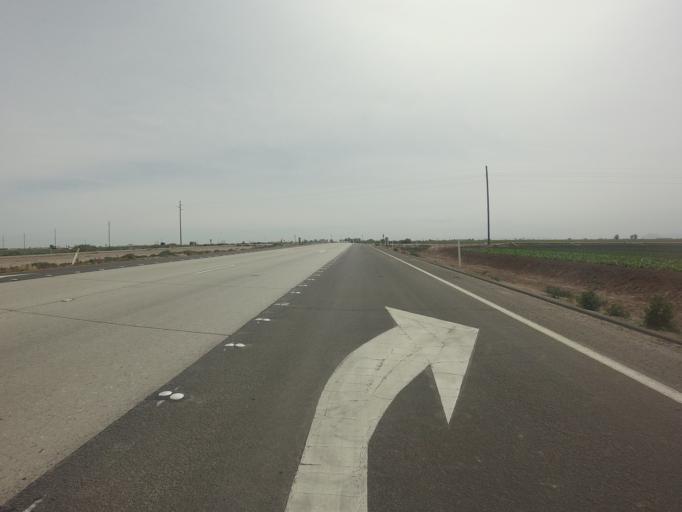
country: US
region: California
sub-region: Imperial County
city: Westmorland
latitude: 33.0309
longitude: -115.6102
